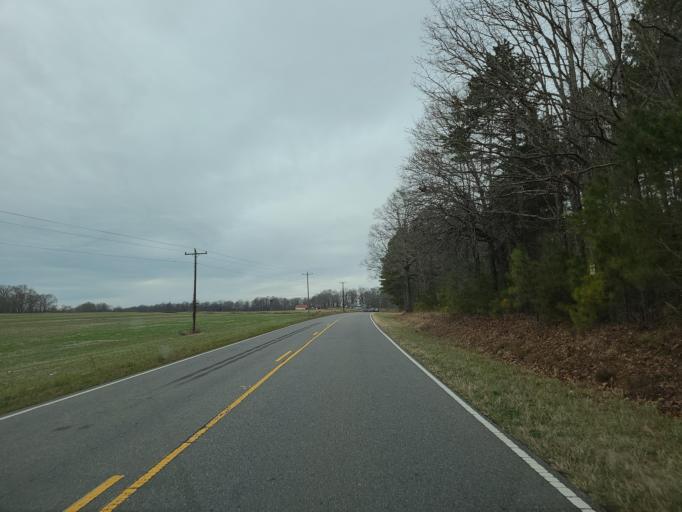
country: US
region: North Carolina
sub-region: Cleveland County
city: Shelby
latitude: 35.3657
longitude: -81.5824
